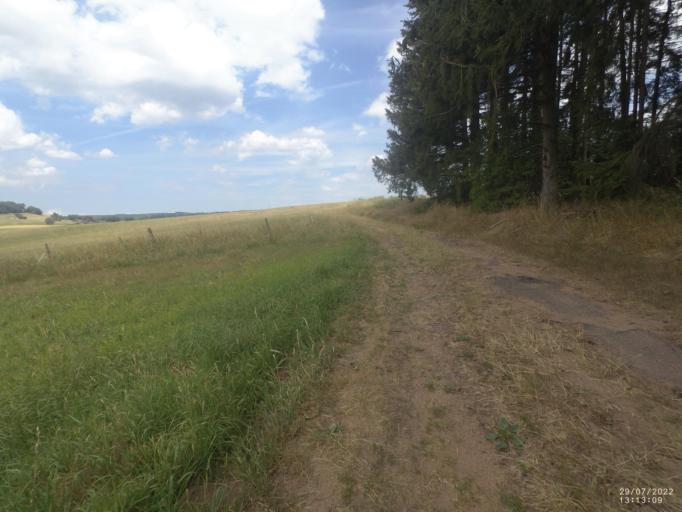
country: DE
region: Rheinland-Pfalz
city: Steffeln
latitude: 50.2766
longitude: 6.5771
